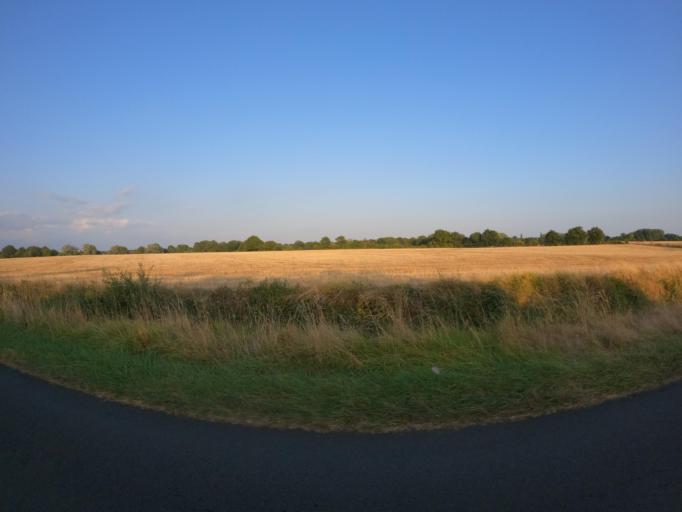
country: FR
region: Pays de la Loire
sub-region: Departement de la Sarthe
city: Brulon
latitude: 47.9397
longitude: -0.2234
